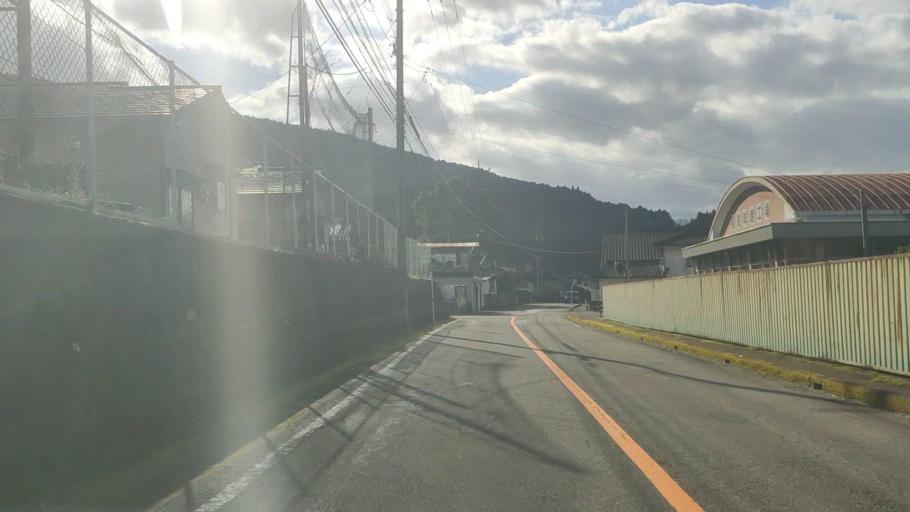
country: JP
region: Kumamoto
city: Hitoyoshi
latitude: 32.3083
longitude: 130.8478
